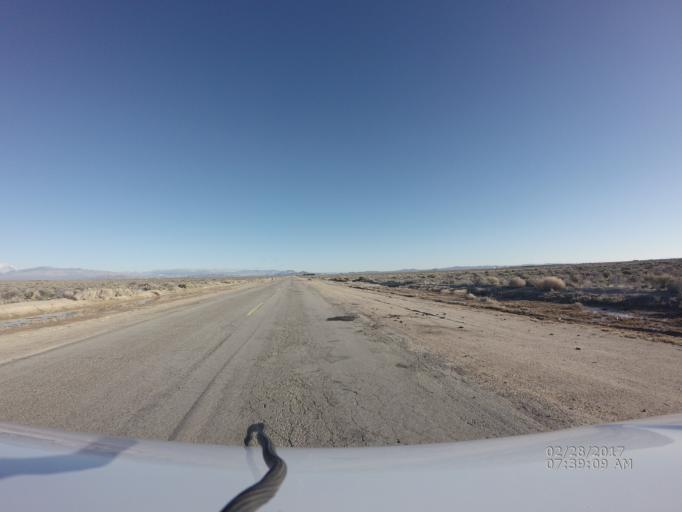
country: US
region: California
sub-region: Los Angeles County
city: Lancaster
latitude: 34.7662
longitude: -118.1845
